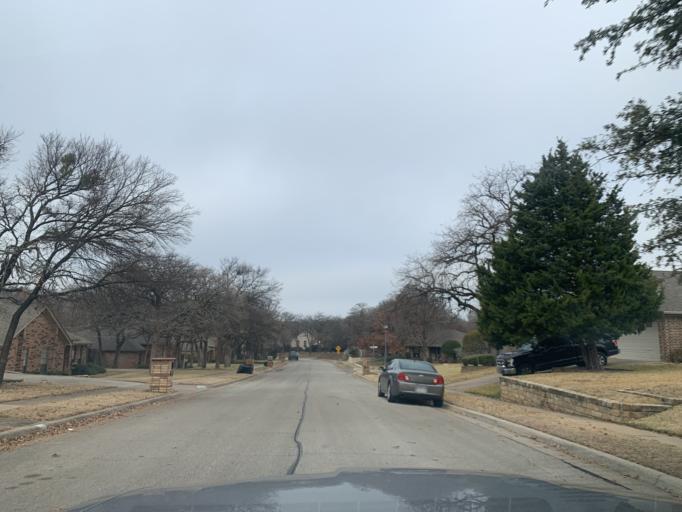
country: US
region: Texas
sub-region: Tarrant County
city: Bedford
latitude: 32.8344
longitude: -97.1490
